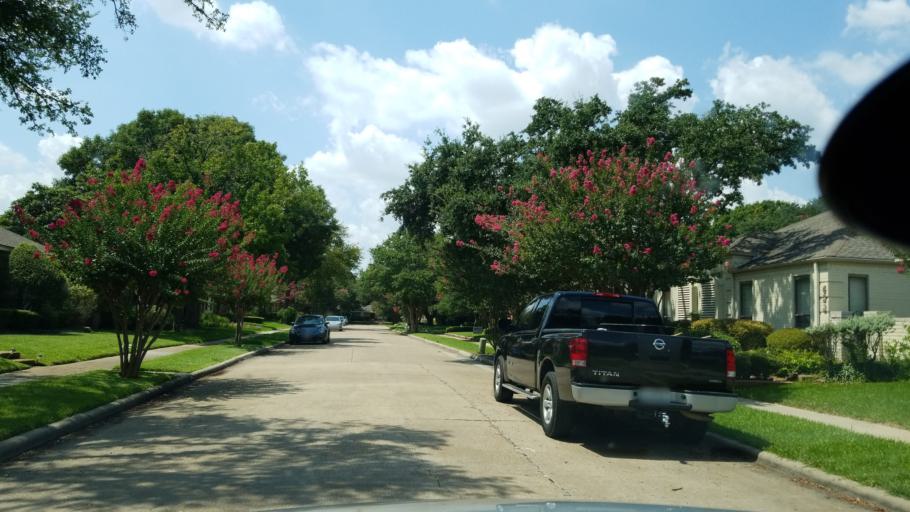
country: US
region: Texas
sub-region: Dallas County
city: Richardson
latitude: 32.9274
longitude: -96.7303
